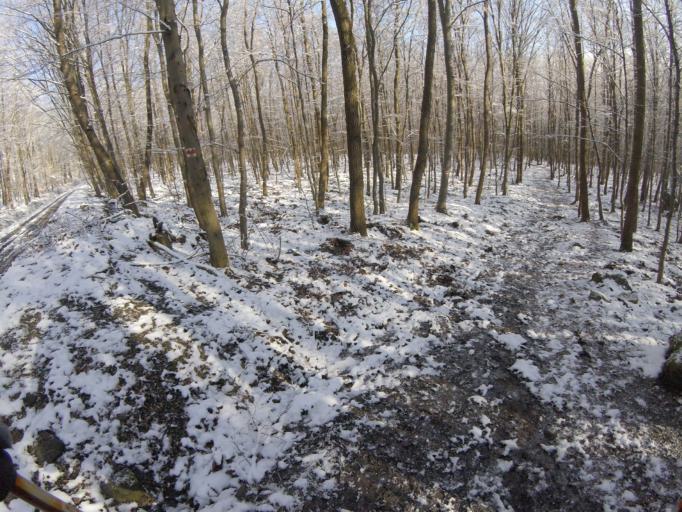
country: HU
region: Komarom-Esztergom
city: Pilismarot
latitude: 47.7411
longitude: 18.8777
